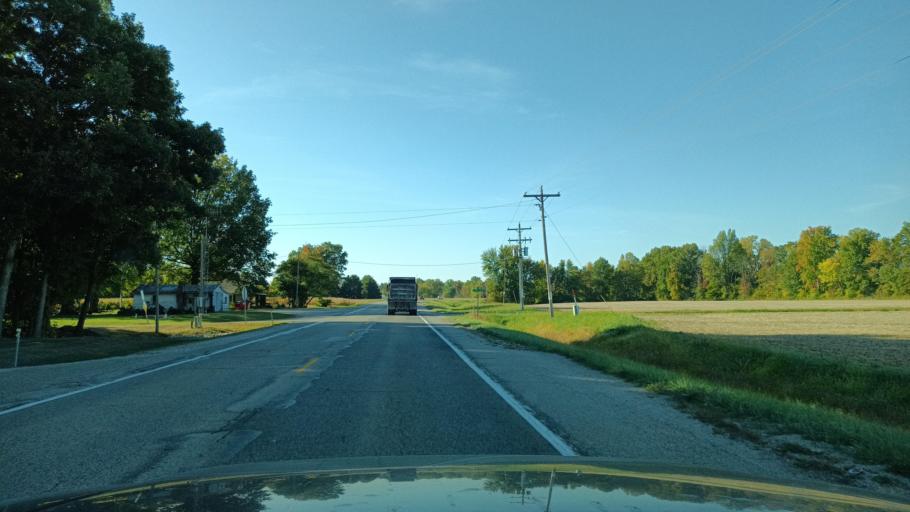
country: US
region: Illinois
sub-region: Clark County
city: Marshall
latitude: 39.4485
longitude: -87.6822
